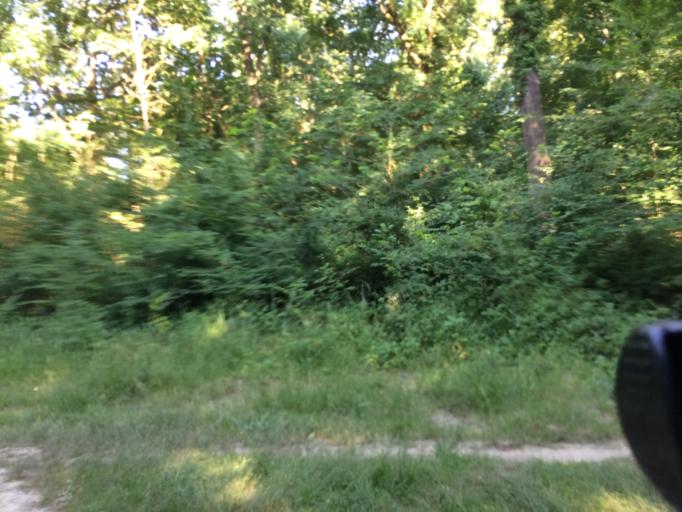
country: FR
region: Ile-de-France
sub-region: Departement de l'Essonne
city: Etiolles
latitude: 48.6487
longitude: 2.4786
